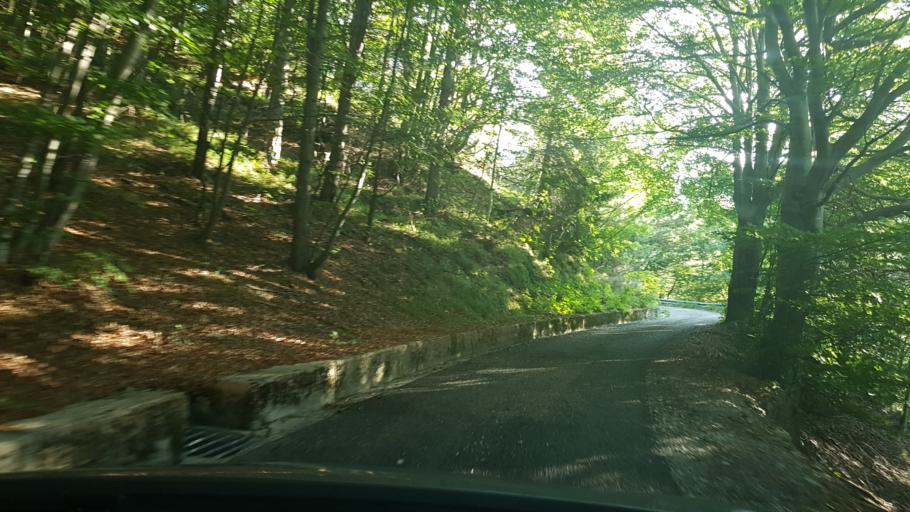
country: IT
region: Friuli Venezia Giulia
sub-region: Provincia di Udine
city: Moggio Udinese
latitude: 46.4452
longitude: 13.2144
